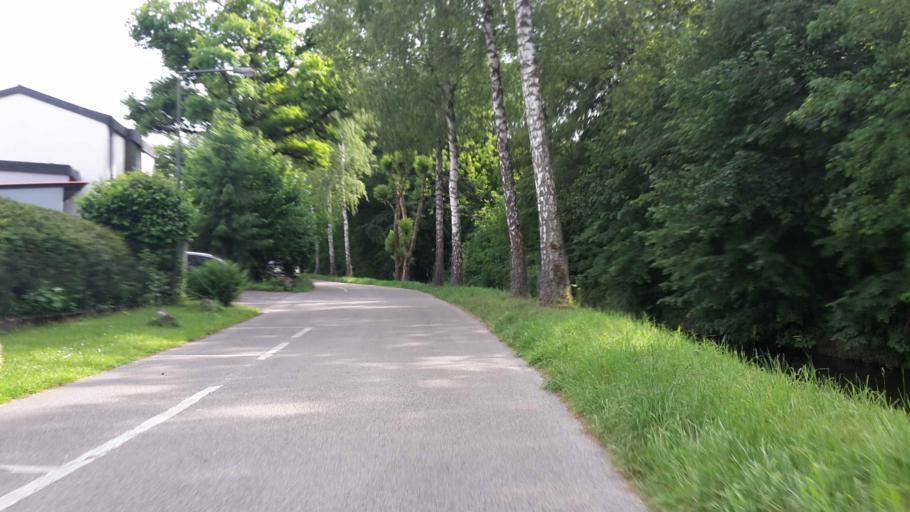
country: DE
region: Bavaria
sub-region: Upper Bavaria
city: Dachau
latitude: 48.2391
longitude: 11.4373
